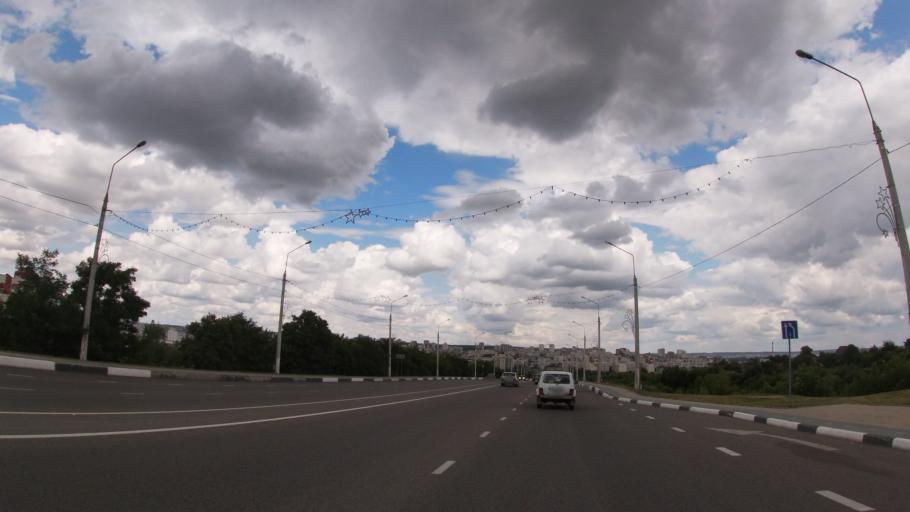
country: RU
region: Belgorod
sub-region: Belgorodskiy Rayon
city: Belgorod
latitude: 50.5816
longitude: 36.5835
